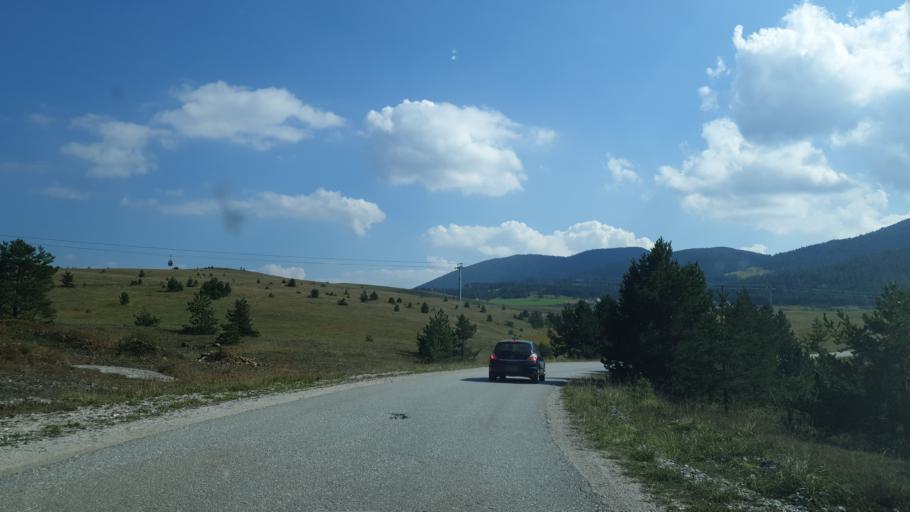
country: RS
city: Zlatibor
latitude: 43.6804
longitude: 19.6561
